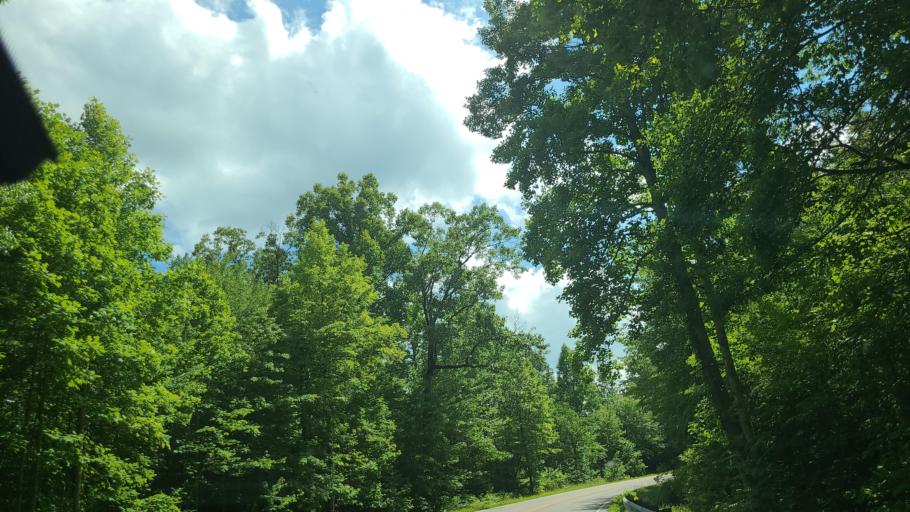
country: US
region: Kentucky
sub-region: Whitley County
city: Williamsburg
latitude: 36.8394
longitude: -84.2670
